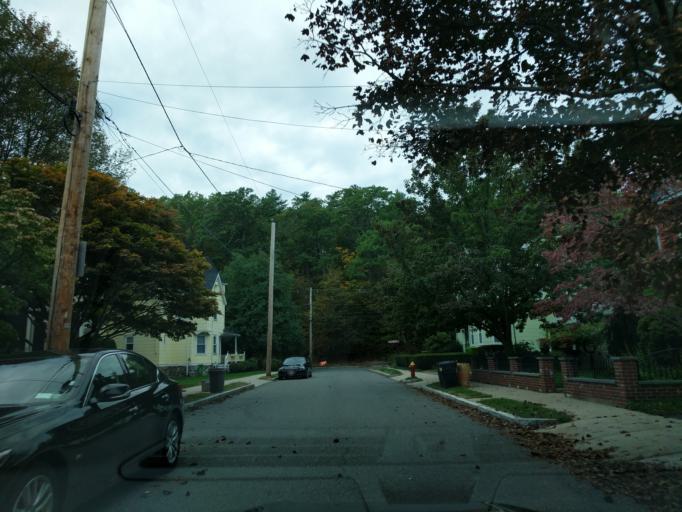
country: US
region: Massachusetts
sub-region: Middlesex County
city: Melrose
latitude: 42.4486
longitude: -71.0744
